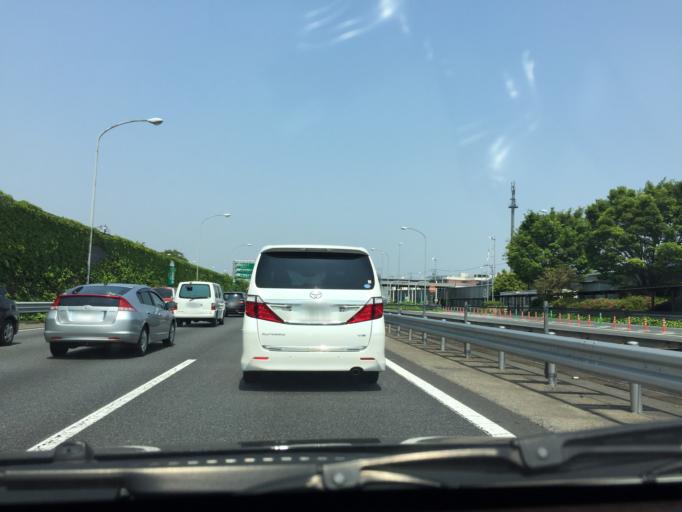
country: JP
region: Saitama
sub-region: Kawaguchi-shi
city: Hatogaya-honcho
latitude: 35.8807
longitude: 139.7291
